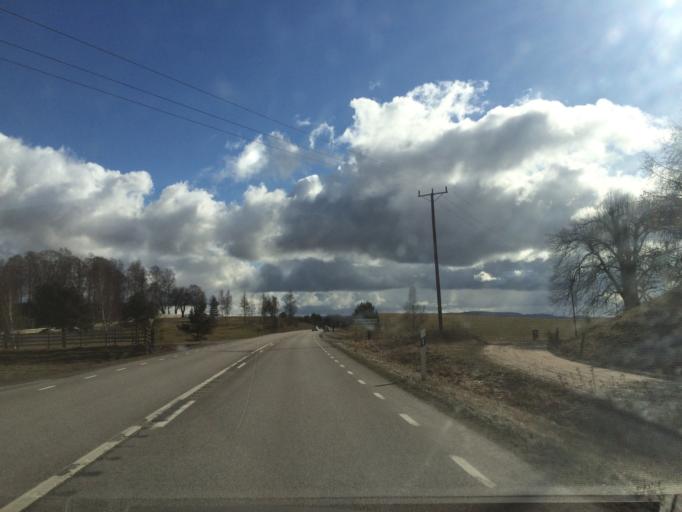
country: SE
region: Vaestra Goetaland
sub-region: Skara Kommun
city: Skara
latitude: 58.2854
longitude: 13.4830
